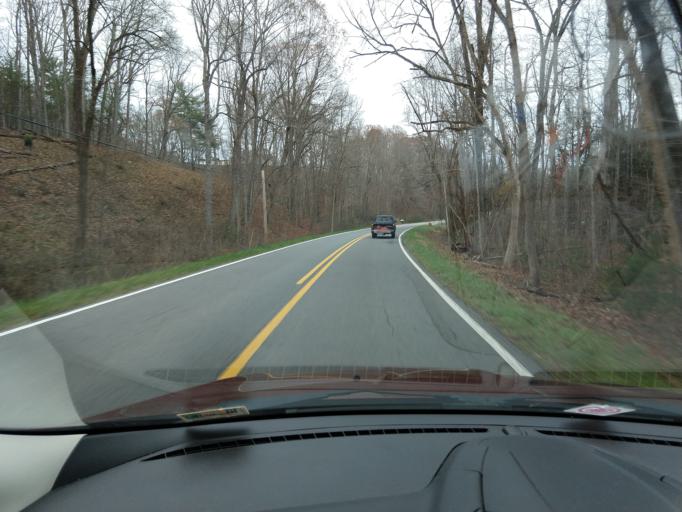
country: US
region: Virginia
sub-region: City of Covington
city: Covington
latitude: 37.7799
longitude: -80.1068
